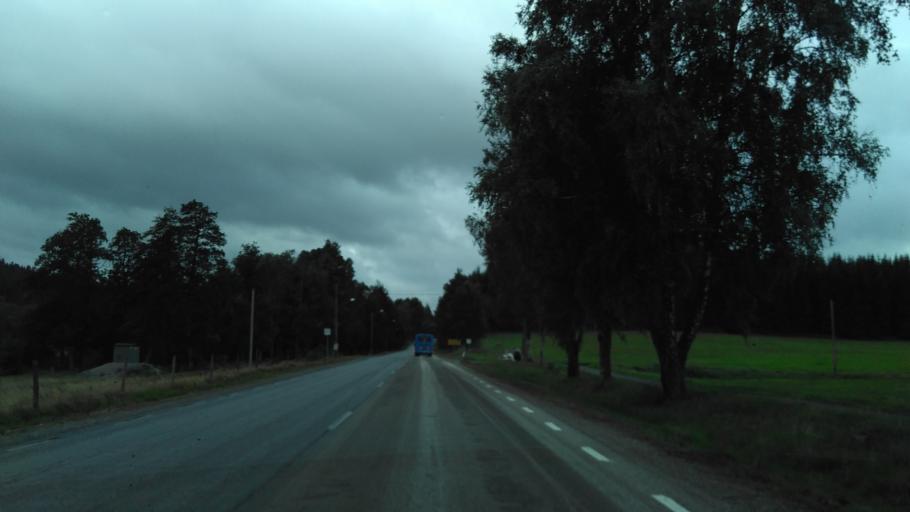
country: SE
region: Vaestra Goetaland
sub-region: Marks Kommun
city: Fritsla
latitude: 57.5660
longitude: 12.8156
